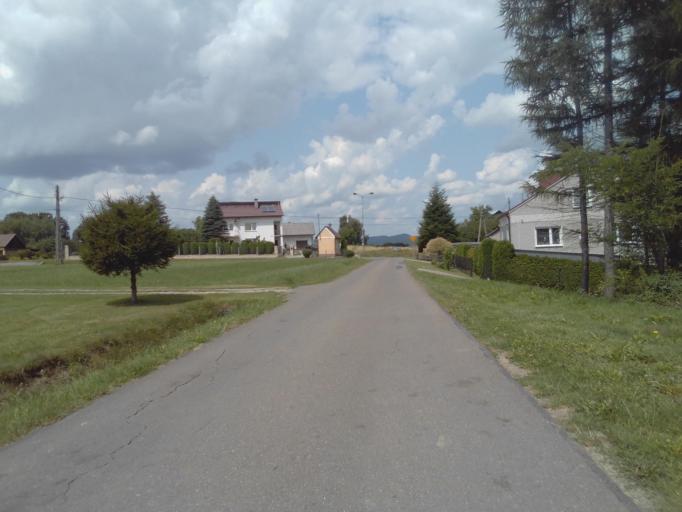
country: PL
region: Subcarpathian Voivodeship
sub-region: Powiat strzyzowski
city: Frysztak
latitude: 49.8233
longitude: 21.6001
